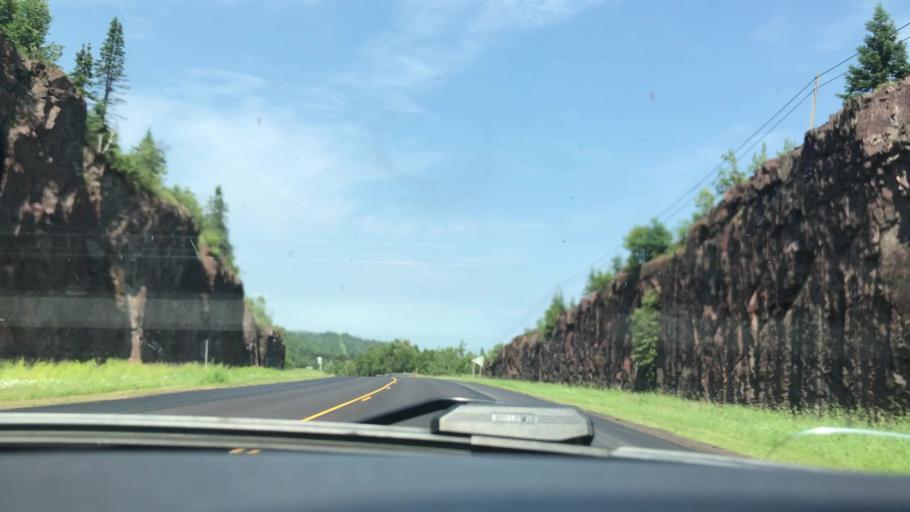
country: US
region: Minnesota
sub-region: Lake County
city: Silver Bay
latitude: 47.3490
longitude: -91.1849
